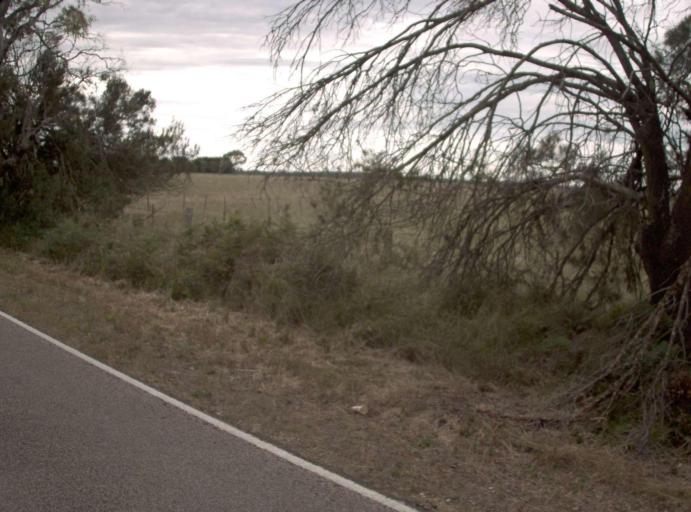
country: AU
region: Victoria
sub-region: East Gippsland
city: Bairnsdale
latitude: -37.9364
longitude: 147.5299
